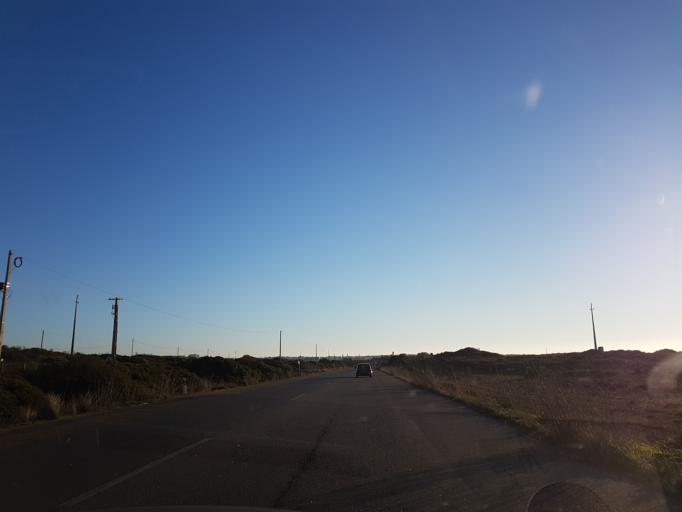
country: PT
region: Faro
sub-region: Vila do Bispo
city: Sagres
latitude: 37.0280
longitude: -8.9369
